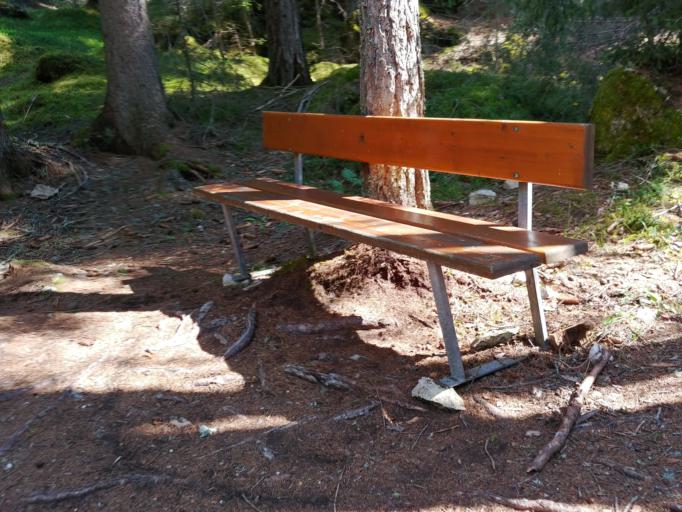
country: IT
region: Trentino-Alto Adige
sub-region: Bolzano
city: Santa Cristina Valgardena
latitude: 46.5676
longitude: 11.7041
